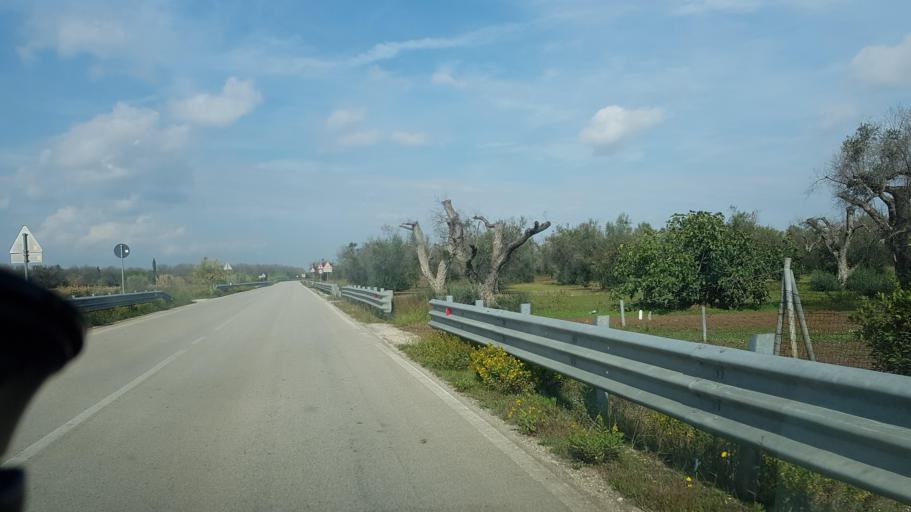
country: IT
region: Apulia
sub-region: Provincia di Brindisi
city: Mesagne
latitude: 40.4937
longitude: 17.8321
